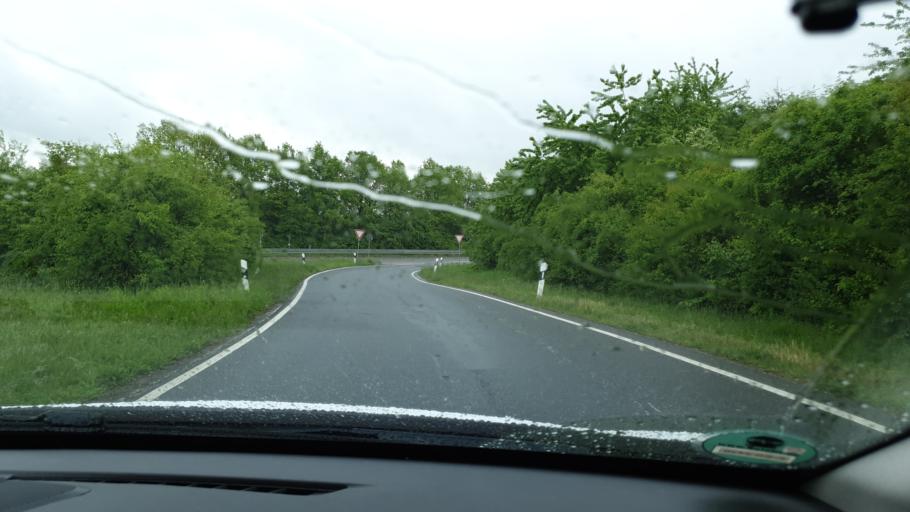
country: DE
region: Hesse
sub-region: Regierungsbezirk Darmstadt
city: Bad Homburg vor der Hoehe
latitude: 50.2151
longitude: 8.6050
